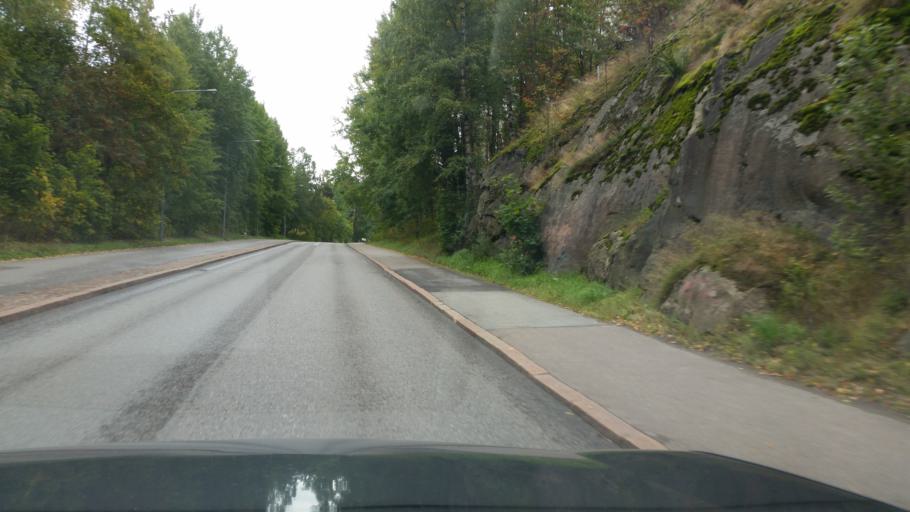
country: FI
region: Uusimaa
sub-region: Helsinki
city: Vantaa
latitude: 60.2386
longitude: 25.0038
